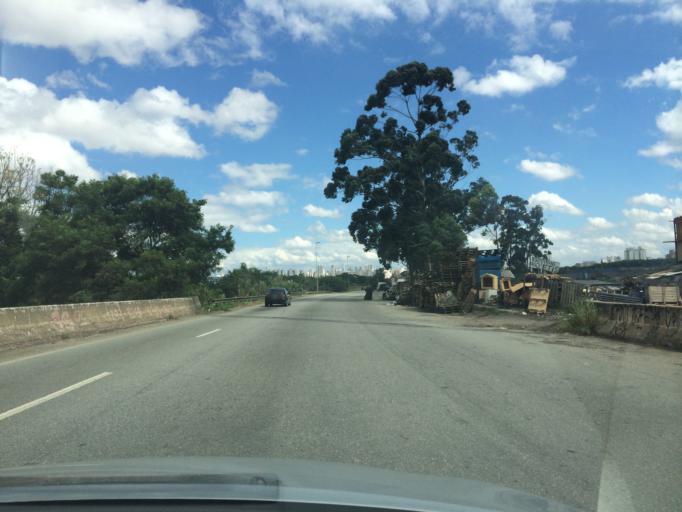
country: BR
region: Sao Paulo
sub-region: Guarulhos
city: Guarulhos
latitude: -23.5073
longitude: -46.5588
